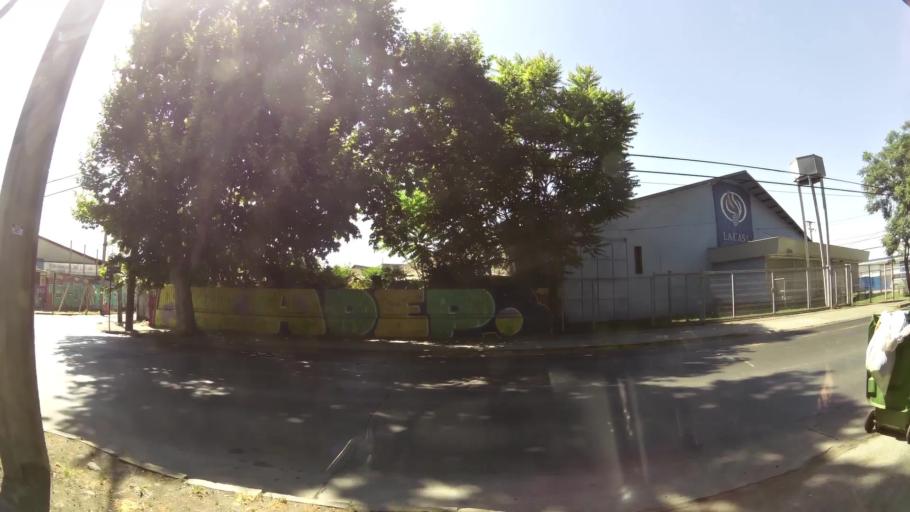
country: CL
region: Santiago Metropolitan
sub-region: Provincia de Maipo
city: San Bernardo
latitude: -33.5570
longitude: -70.6773
